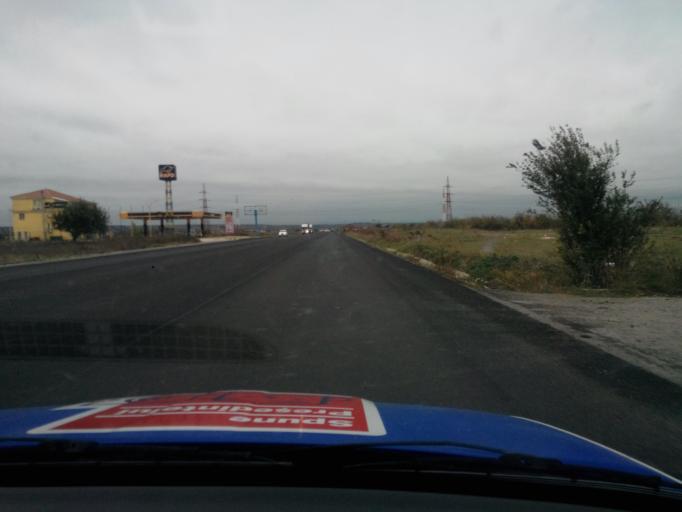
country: RO
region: Giurgiu
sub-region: Comuna Fratesti
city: Remus
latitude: 43.9501
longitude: 25.9808
